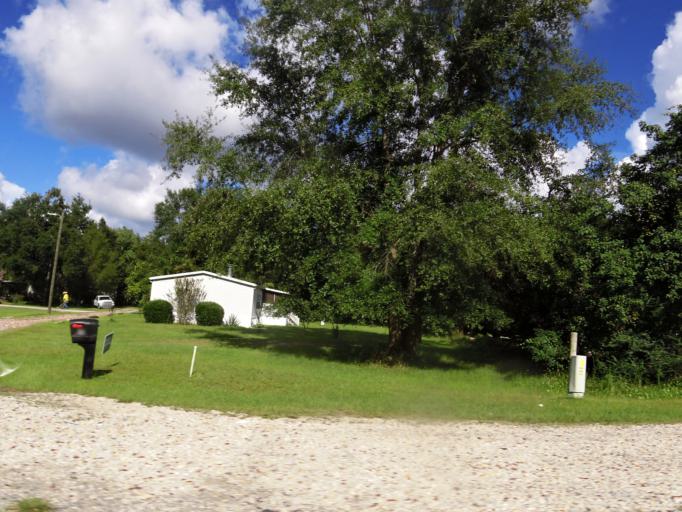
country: US
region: Georgia
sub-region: Camden County
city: Kingsland
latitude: 30.8126
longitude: -81.6927
